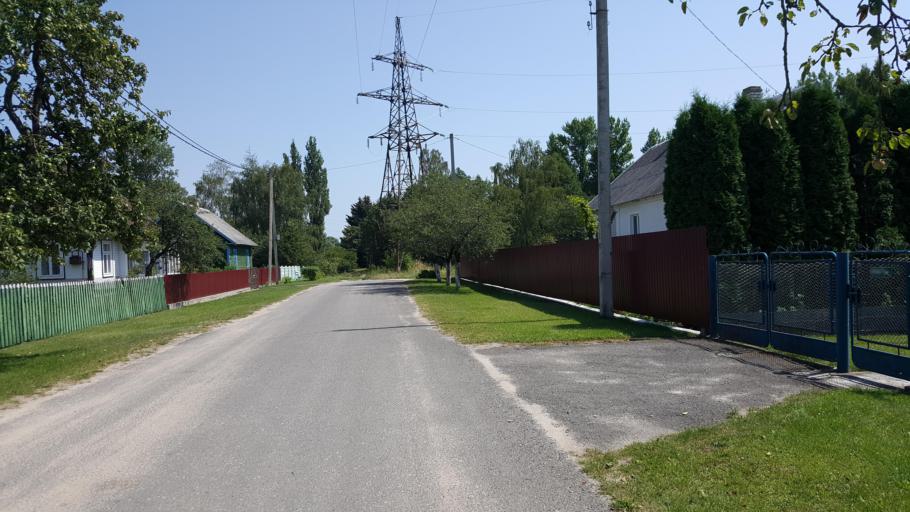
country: BY
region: Brest
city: Zhabinka
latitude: 52.1915
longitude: 24.0149
